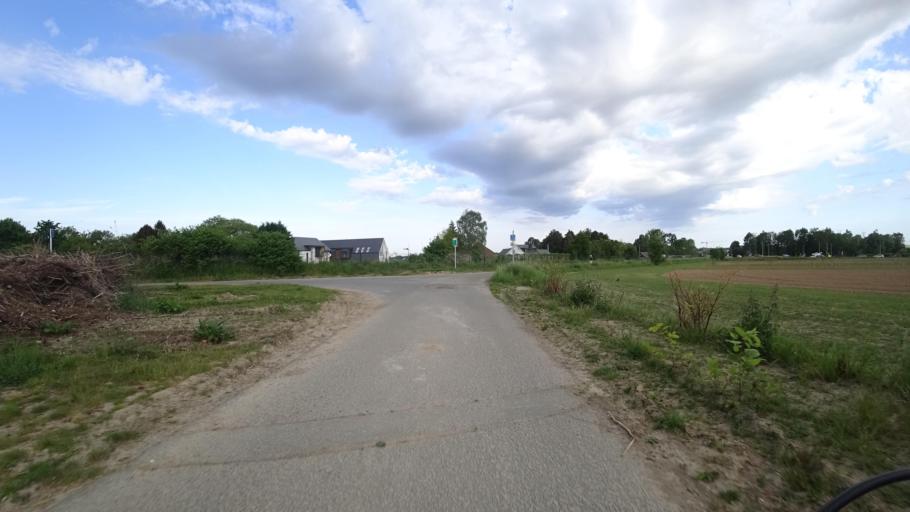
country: BE
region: Wallonia
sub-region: Province de Namur
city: Gembloux
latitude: 50.5611
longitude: 4.7066
